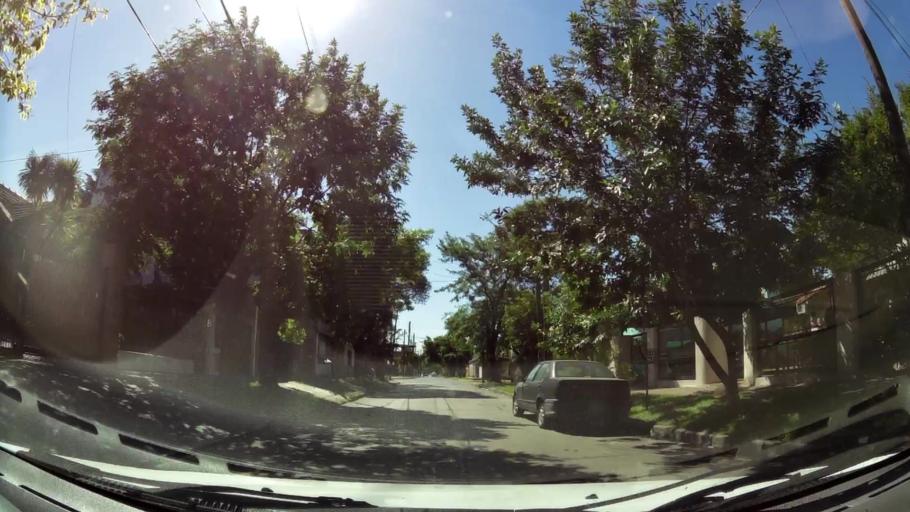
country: AR
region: Buenos Aires
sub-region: Partido de General San Martin
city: General San Martin
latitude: -34.5442
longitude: -58.5711
